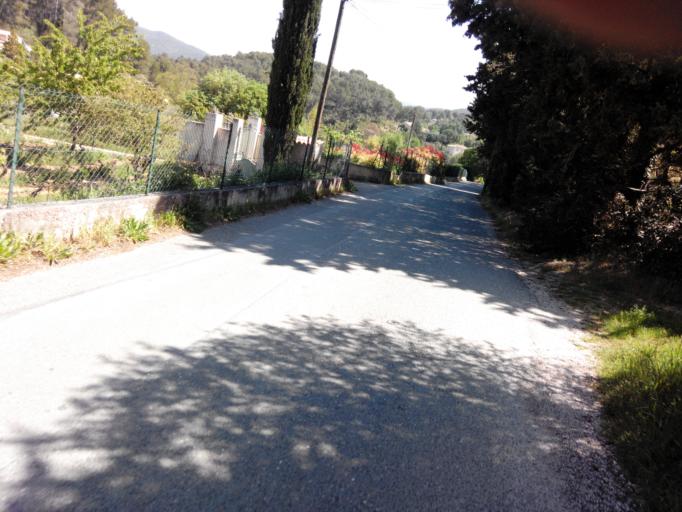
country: FR
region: Provence-Alpes-Cote d'Azur
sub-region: Departement des Bouches-du-Rhone
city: Auriol
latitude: 43.3584
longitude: 5.6353
